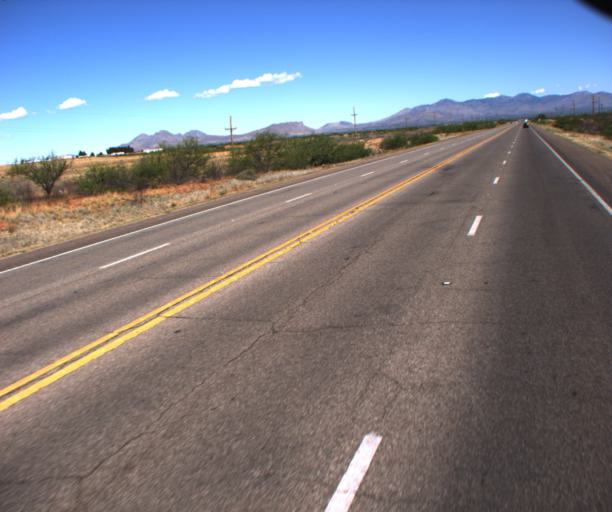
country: US
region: Arizona
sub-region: Cochise County
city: Sierra Vista
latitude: 31.5871
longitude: -110.3212
